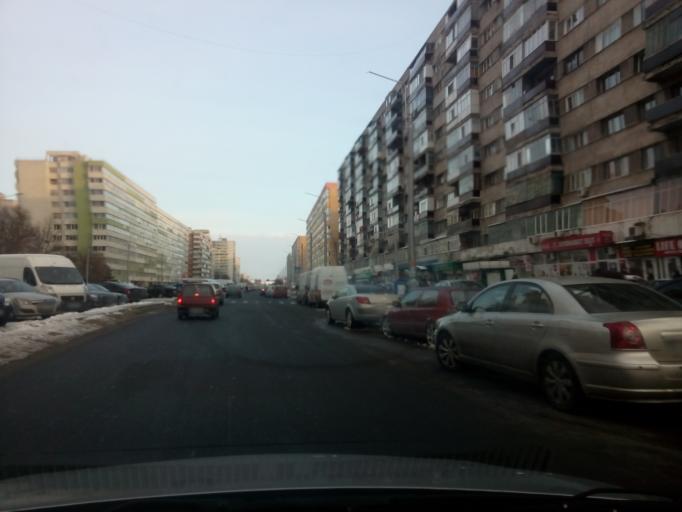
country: RO
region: Ilfov
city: Dobroesti
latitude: 44.4419
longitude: 26.1743
